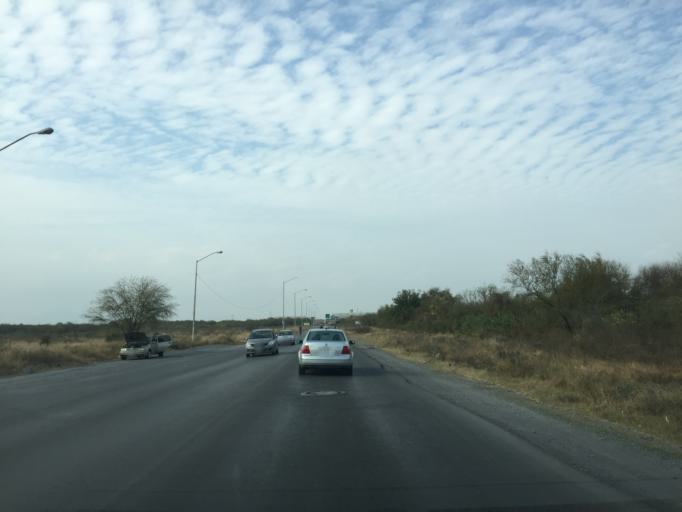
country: MX
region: Nuevo Leon
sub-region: Apodaca
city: Fraccionamiento Cosmopolis Octavo Sector
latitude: 25.8073
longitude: -100.2496
